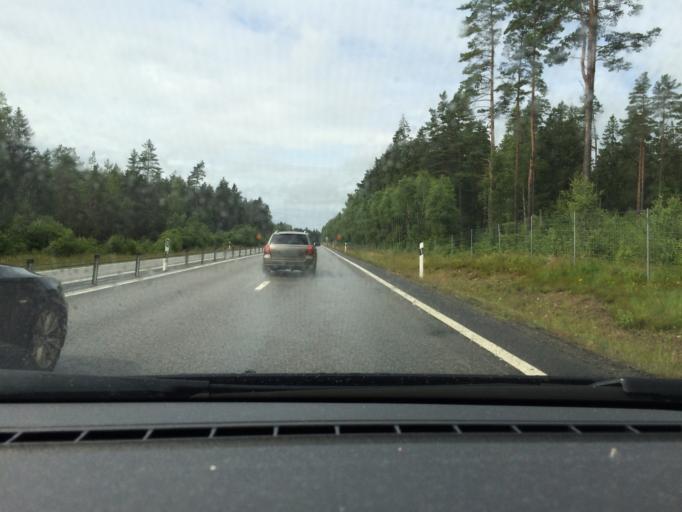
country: SE
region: Joenkoeping
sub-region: Varnamo Kommun
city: Forsheda
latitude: 57.1668
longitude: 13.8854
